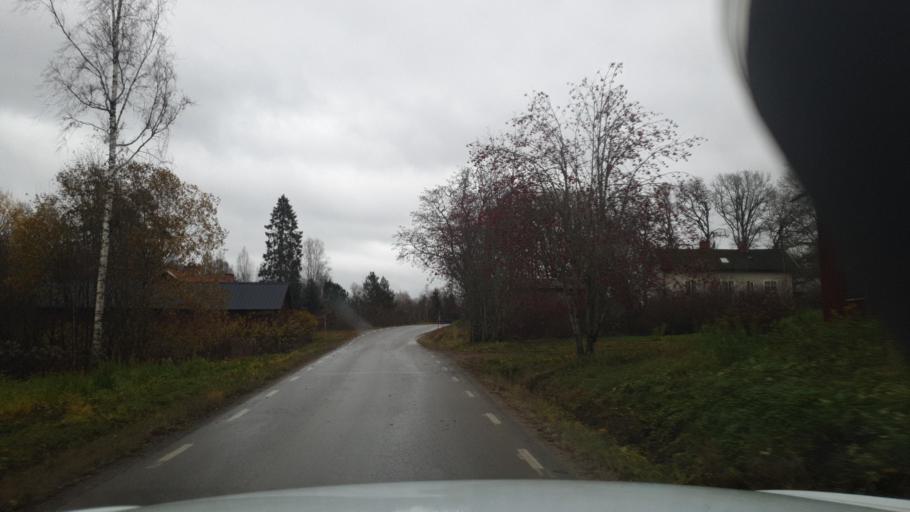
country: SE
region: Vaermland
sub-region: Arvika Kommun
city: Arvika
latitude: 59.8176
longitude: 12.5583
